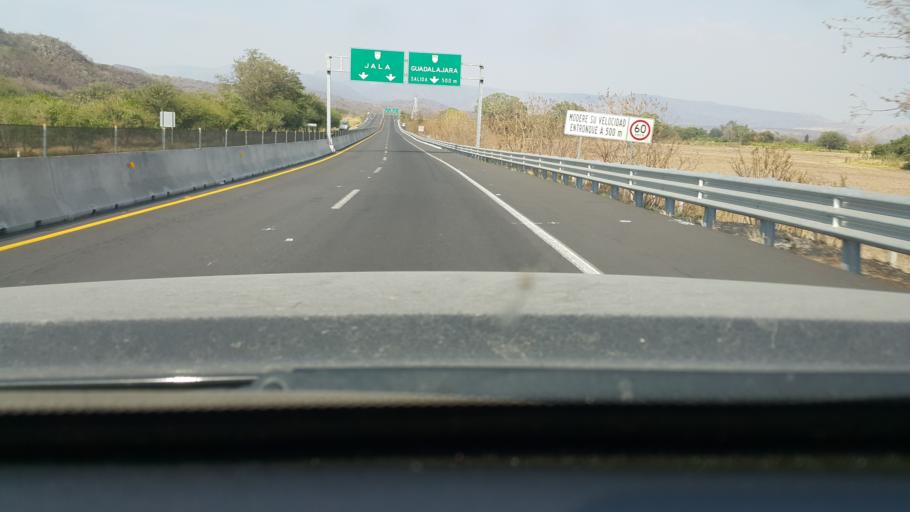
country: MX
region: Nayarit
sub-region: Ahuacatlan
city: Ahuacatlan
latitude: 21.0564
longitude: -104.5152
